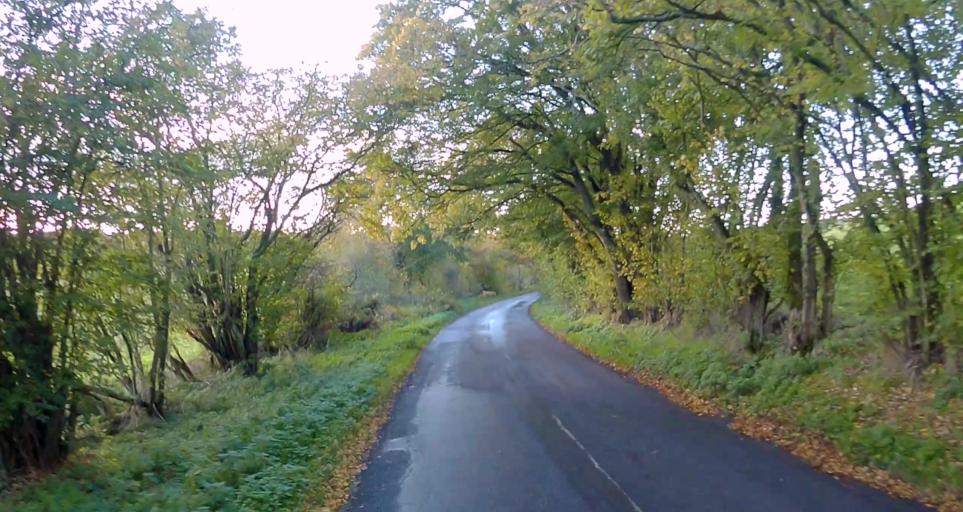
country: GB
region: England
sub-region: Hampshire
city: Basingstoke
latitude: 51.1905
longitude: -1.0780
